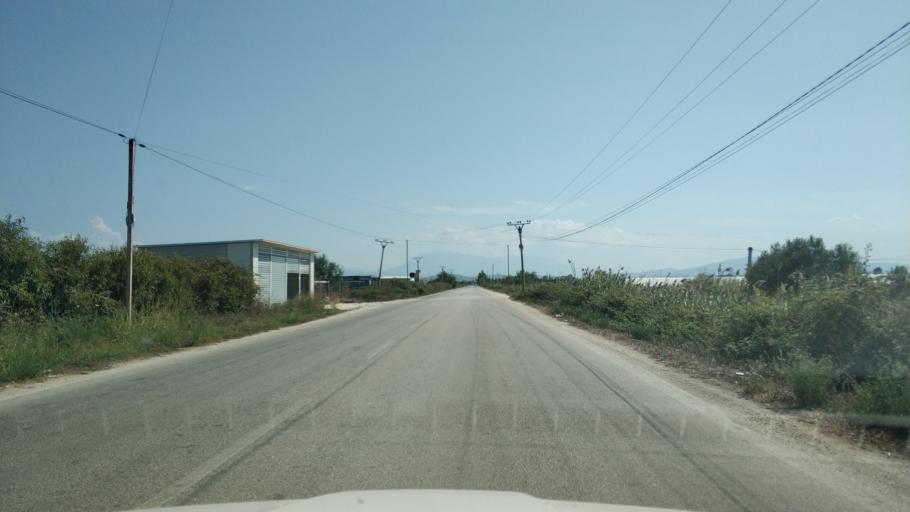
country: AL
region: Fier
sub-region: Rrethi i Lushnjes
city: Krutja e Poshtme
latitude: 40.8845
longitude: 19.6553
